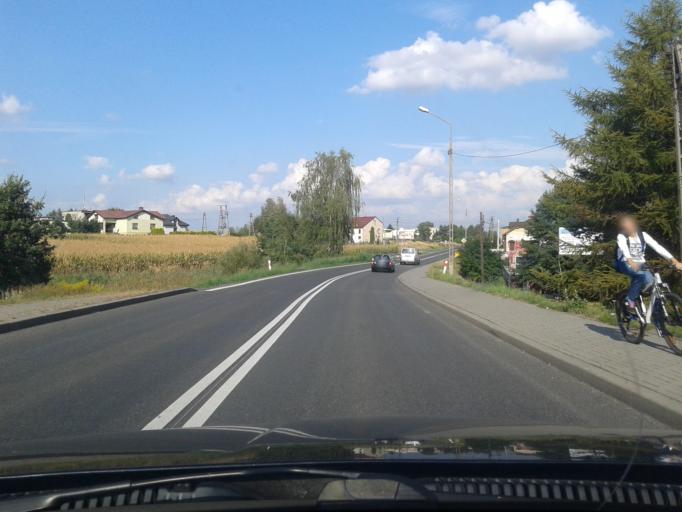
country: PL
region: Silesian Voivodeship
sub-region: Powiat wodzislawski
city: Gorzyce
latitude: 49.9613
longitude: 18.4036
